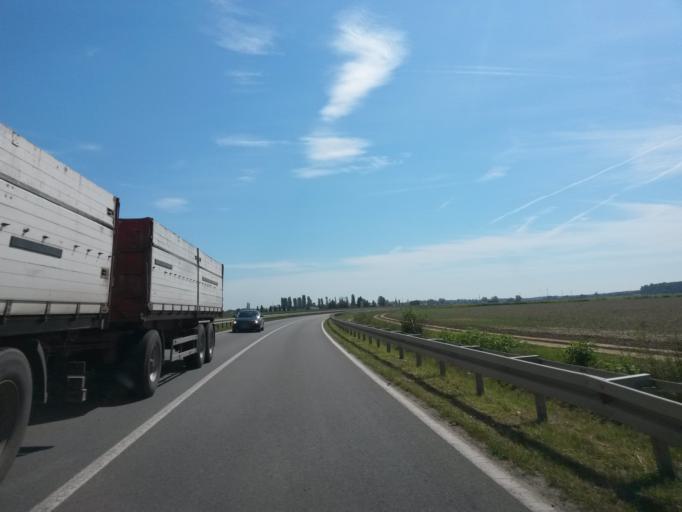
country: HR
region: Vukovarsko-Srijemska
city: Vinkovci
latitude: 45.2745
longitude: 18.7877
